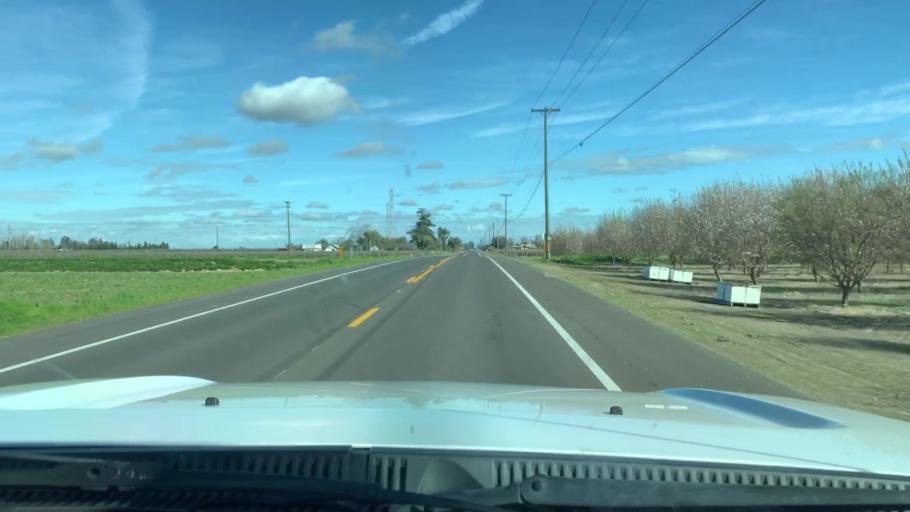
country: US
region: California
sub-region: Fresno County
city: Fowler
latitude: 36.5899
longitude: -119.6825
